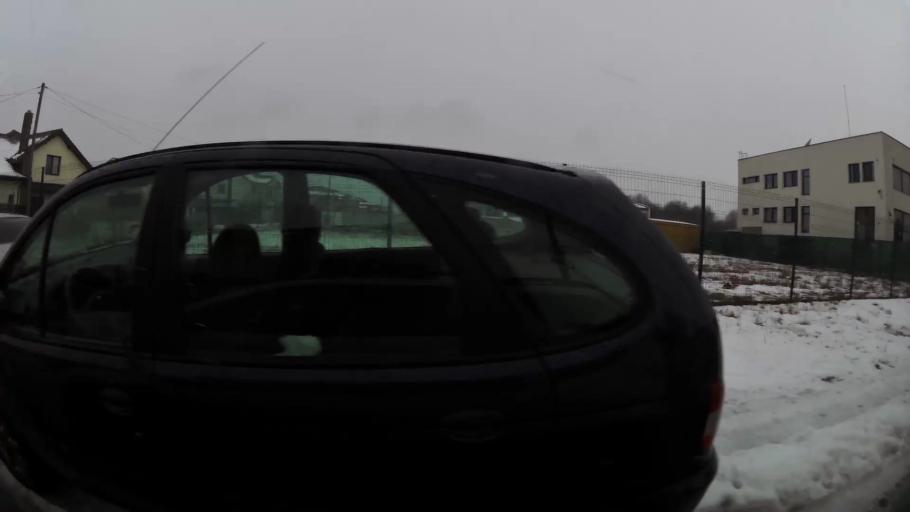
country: RO
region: Ilfov
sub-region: Comuna Mogosoaia
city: Mogosoaia
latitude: 44.5086
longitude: 26.0150
